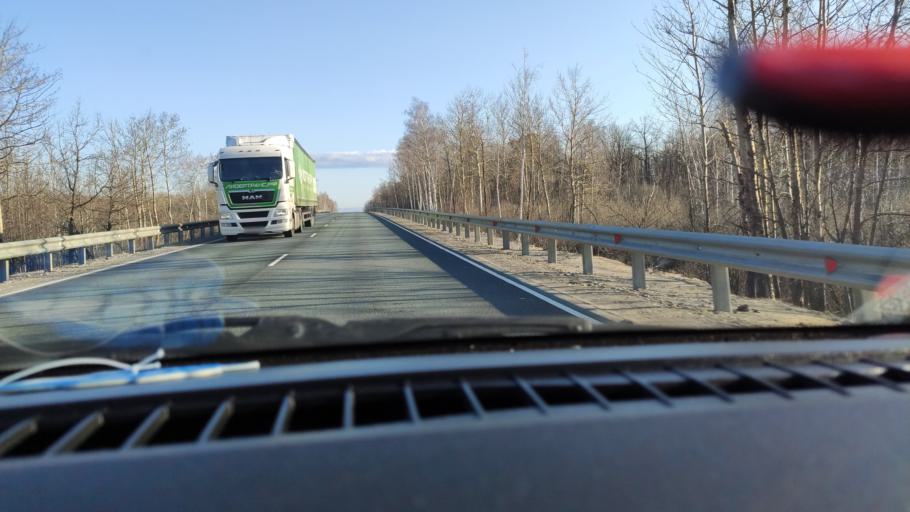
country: RU
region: Saratov
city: Khvalynsk
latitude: 52.4934
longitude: 48.0143
